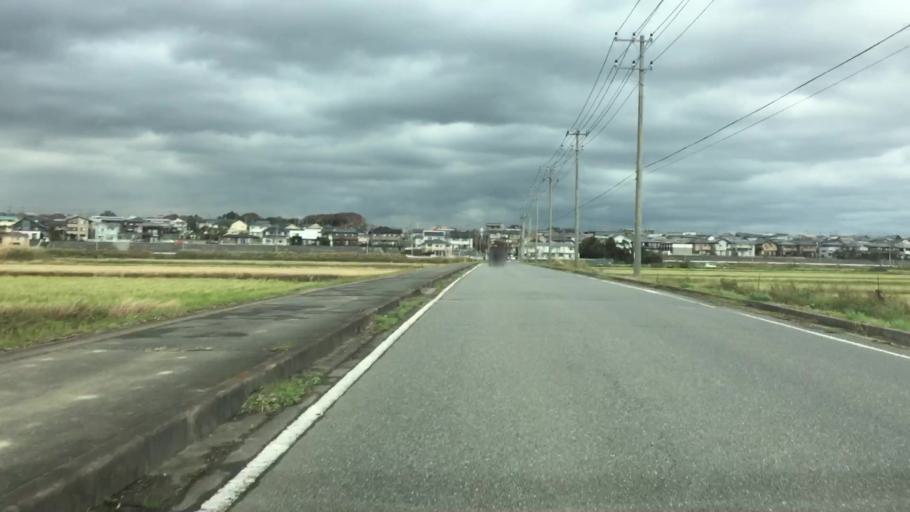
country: JP
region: Ibaraki
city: Toride
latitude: 35.8555
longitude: 140.1021
